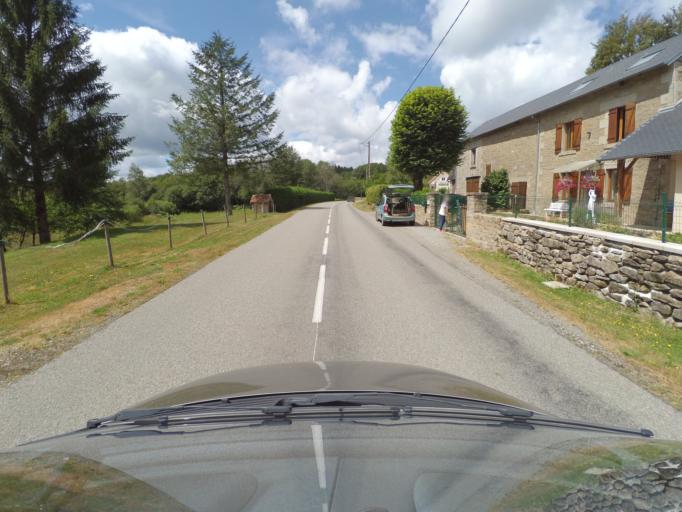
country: FR
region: Limousin
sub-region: Departement de la Creuse
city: Bourganeuf
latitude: 45.9265
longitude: 1.8398
